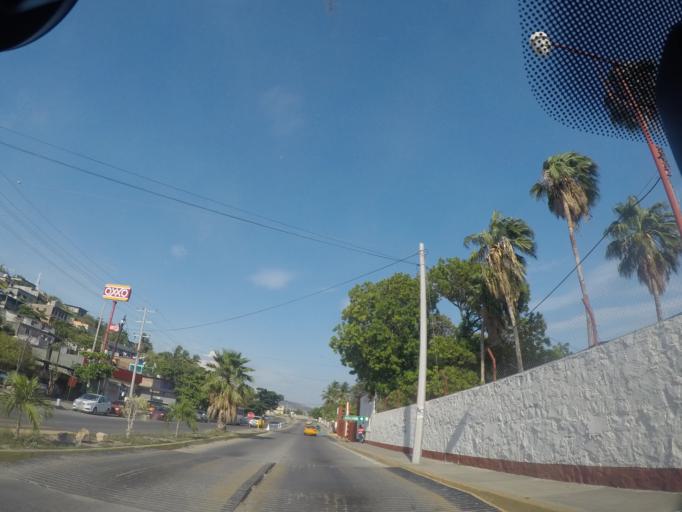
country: MX
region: Oaxaca
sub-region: Salina Cruz
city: Salina Cruz
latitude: 16.1727
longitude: -95.2013
